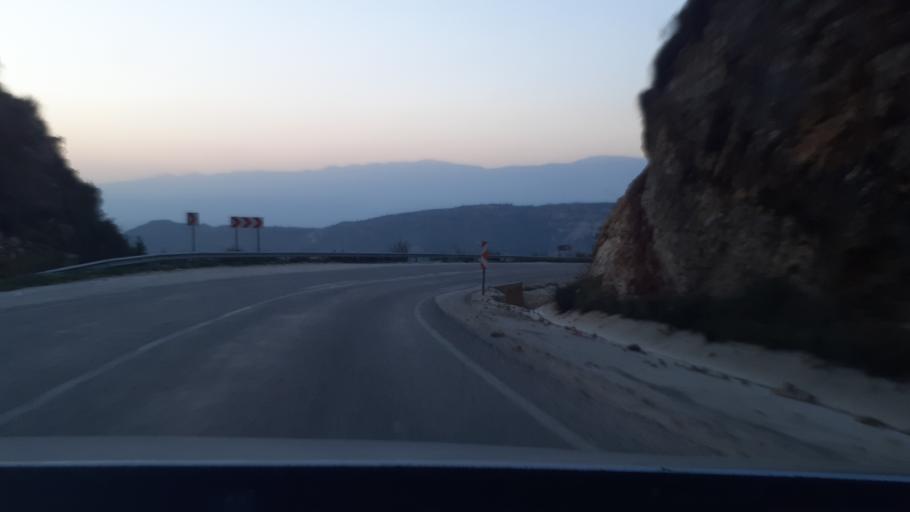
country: TR
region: Hatay
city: Dursunlu
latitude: 36.1685
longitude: 36.1868
